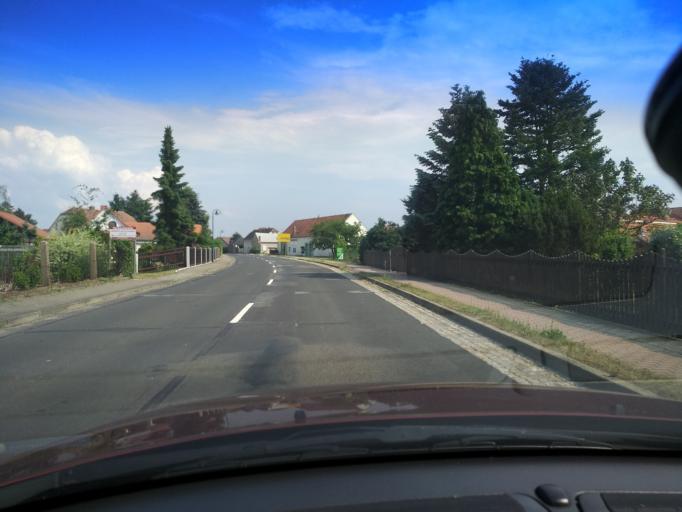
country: DE
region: Saxony
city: Klitten
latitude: 51.3497
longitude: 14.6011
